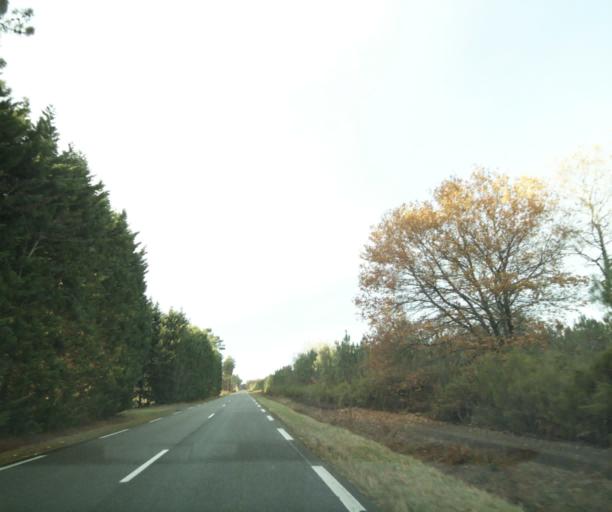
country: FR
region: Aquitaine
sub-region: Departement des Landes
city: Gabarret
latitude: 44.0269
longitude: -0.0271
